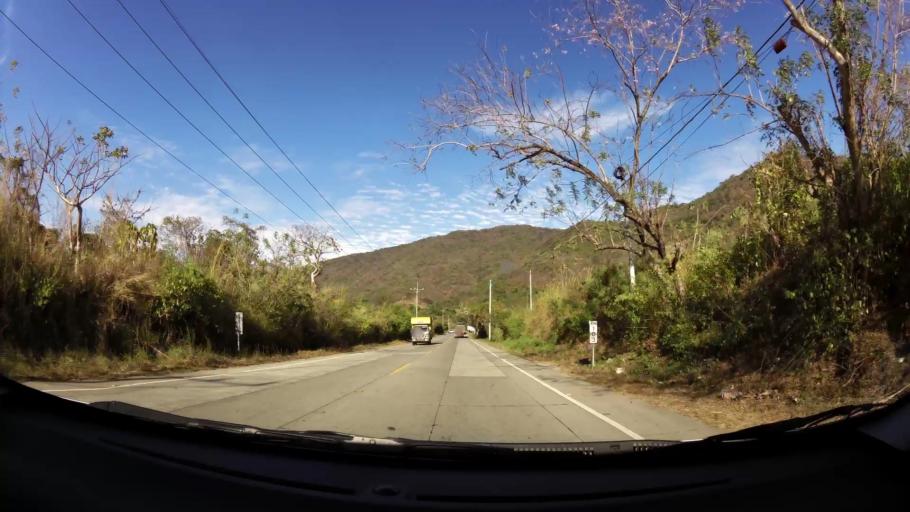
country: SV
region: Santa Ana
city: Metapan
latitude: 14.2488
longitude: -89.4674
